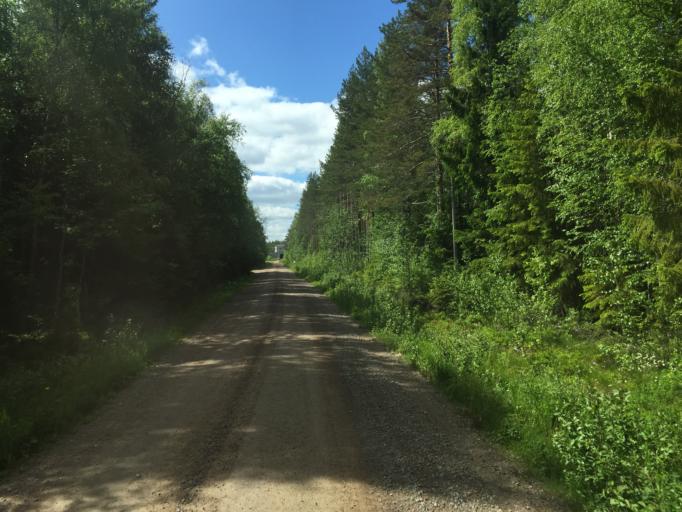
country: SE
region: Dalarna
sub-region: Vansbro Kommun
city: Vansbro
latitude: 60.4502
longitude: 14.1548
